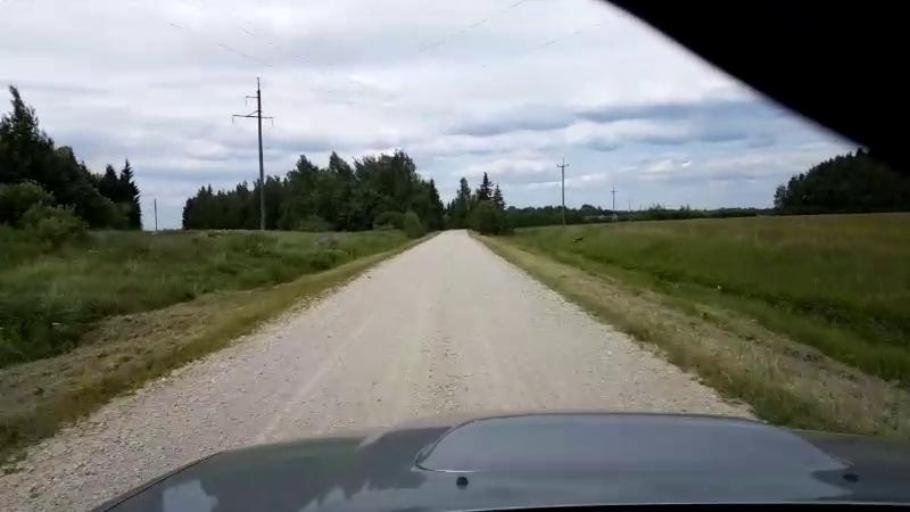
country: EE
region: Paernumaa
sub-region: Halinga vald
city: Parnu-Jaagupi
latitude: 58.5223
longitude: 24.5867
